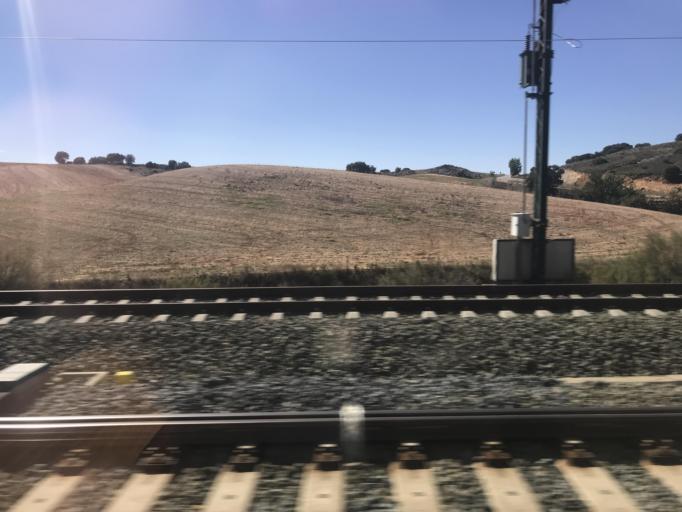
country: ES
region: Castille-La Mancha
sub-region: Provincia de Cuenca
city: Cuenca
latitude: 40.0305
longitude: -2.1387
